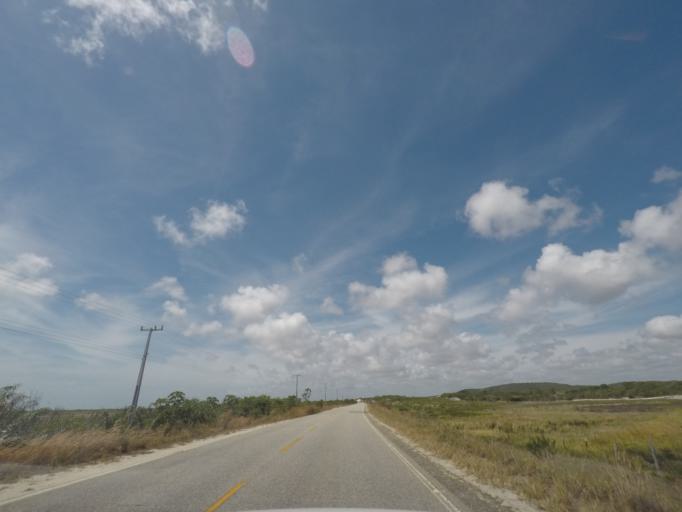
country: BR
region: Sergipe
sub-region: Sao Cristovao
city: Sao Cristovao
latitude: -11.1681
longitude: -37.2078
